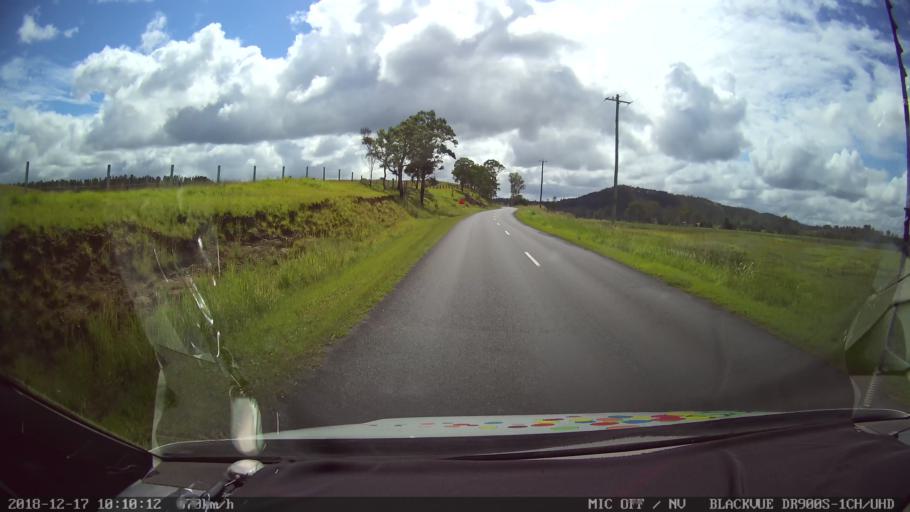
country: AU
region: New South Wales
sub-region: Clarence Valley
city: Gordon
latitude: -28.8875
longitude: 152.5536
